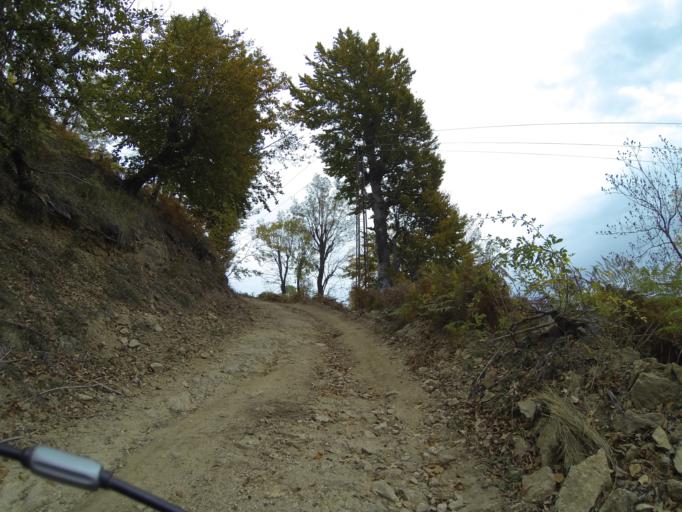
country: RO
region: Gorj
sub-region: Comuna Pades
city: Closani
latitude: 45.1084
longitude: 22.8460
